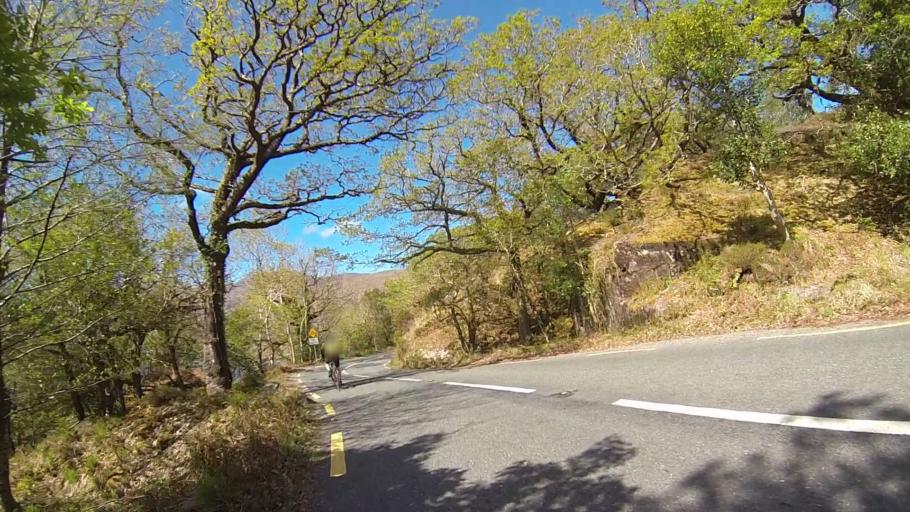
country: IE
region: Munster
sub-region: Ciarrai
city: Cill Airne
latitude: 51.9798
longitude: -9.5743
